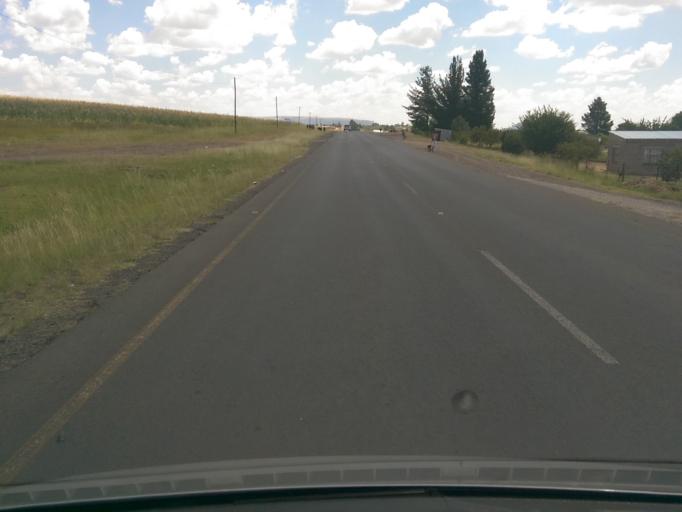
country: LS
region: Maseru
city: Maseru
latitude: -29.4080
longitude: 27.6055
